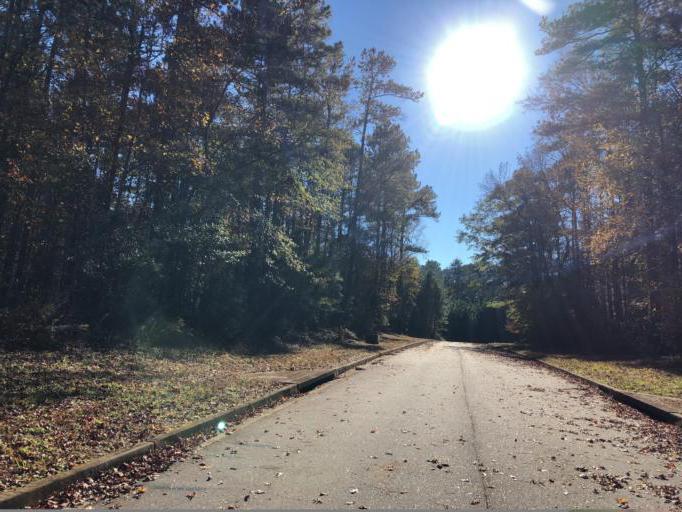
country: US
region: Georgia
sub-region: Spalding County
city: Experiment
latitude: 33.2820
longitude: -84.3018
